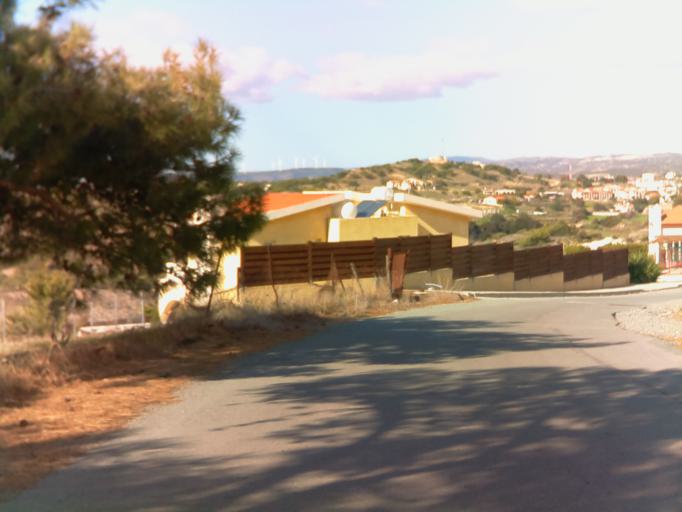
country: CY
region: Limassol
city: Pissouri
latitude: 34.6563
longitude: 32.6967
